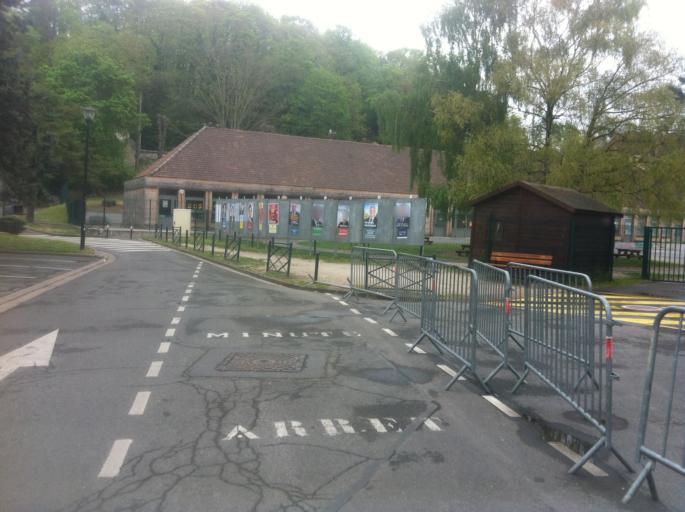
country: FR
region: Ile-de-France
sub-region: Departement du Val-d'Oise
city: Auvers-sur-Oise
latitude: 49.0715
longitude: 2.1700
